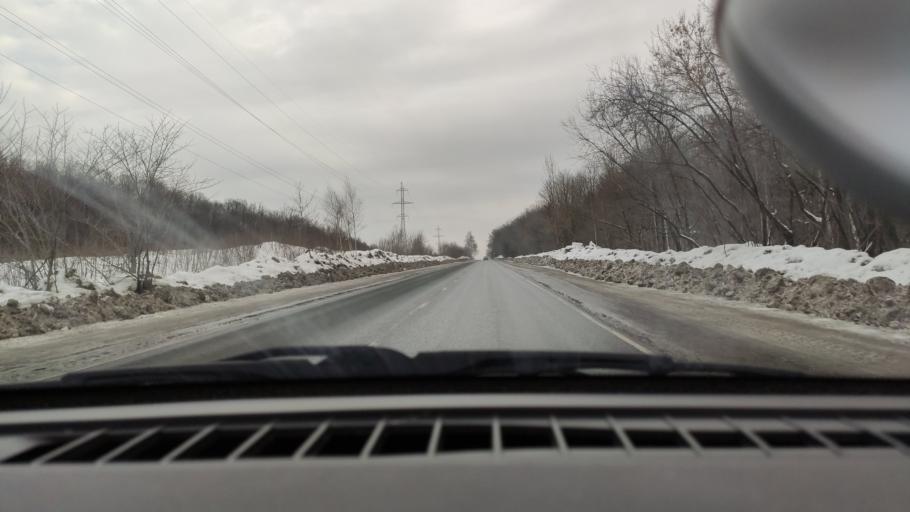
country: RU
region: Samara
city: Novosemeykino
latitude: 53.3443
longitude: 50.2448
